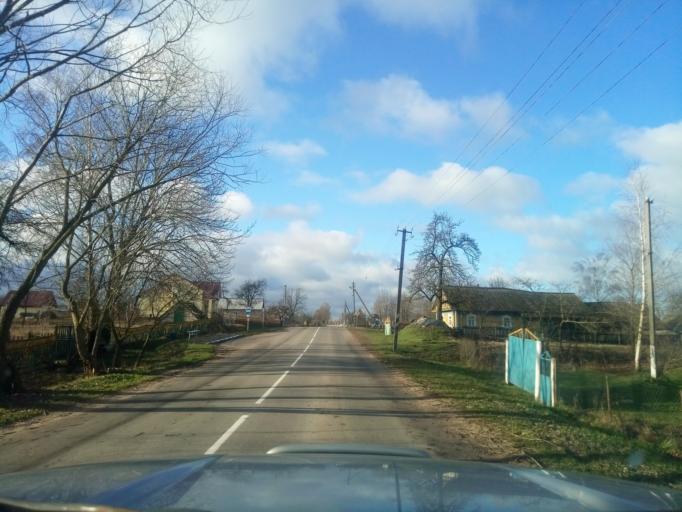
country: BY
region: Minsk
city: Tsimkavichy
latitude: 53.1754
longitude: 26.9621
